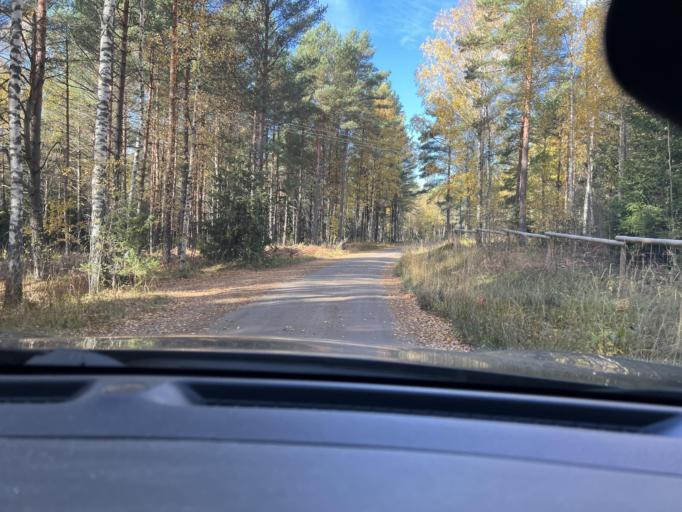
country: SE
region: Stockholm
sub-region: Vallentuna Kommun
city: Vallentuna
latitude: 59.5097
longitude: 18.1261
